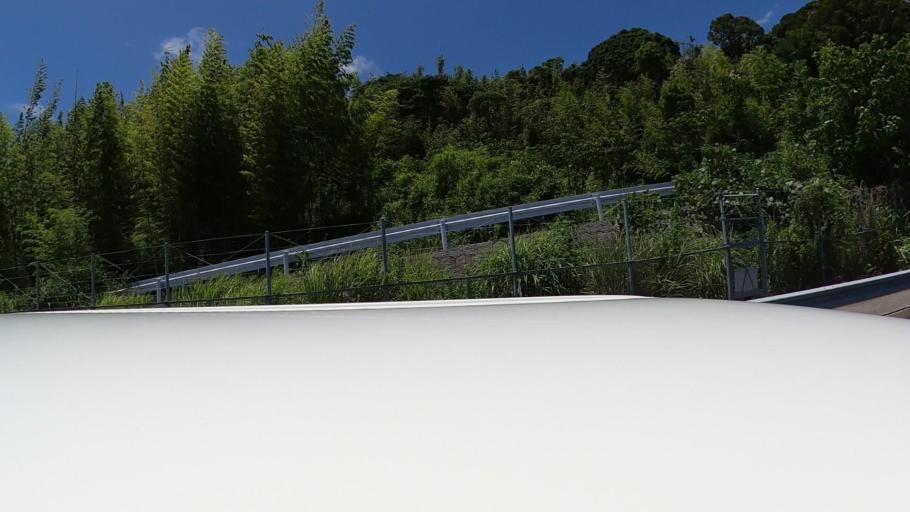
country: JP
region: Miyazaki
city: Nobeoka
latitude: 32.3835
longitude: 131.6206
